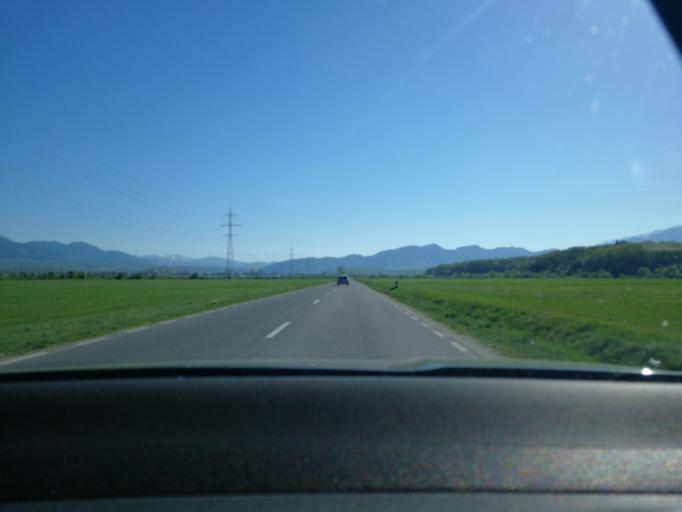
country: RO
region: Brasov
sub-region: Oras Rasnov
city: Rasnov
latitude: 45.5928
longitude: 25.4149
